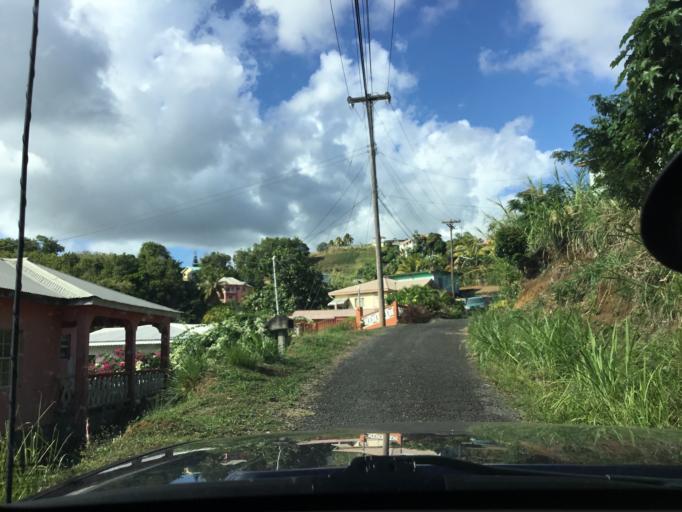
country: VC
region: Saint George
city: Kingstown
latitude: 13.1486
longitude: -61.1790
